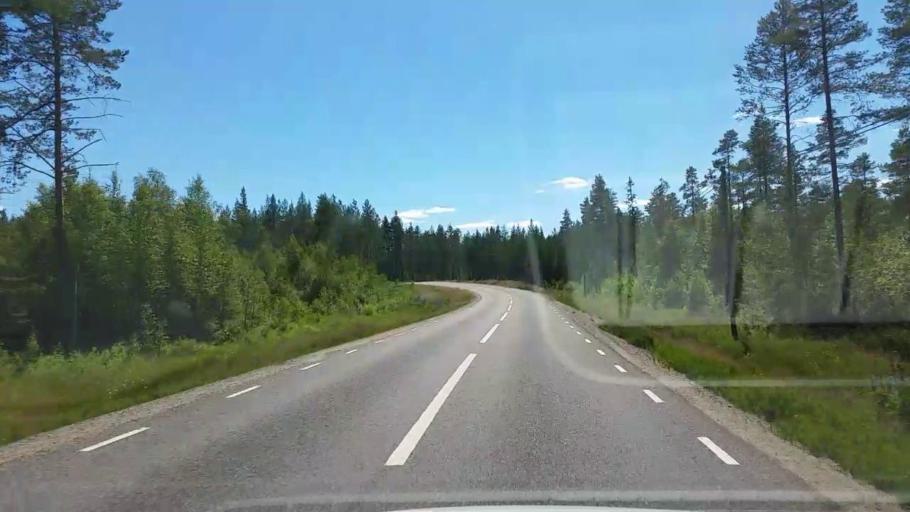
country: SE
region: Gaevleborg
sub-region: Ovanakers Kommun
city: Edsbyn
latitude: 61.4457
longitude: 15.7106
